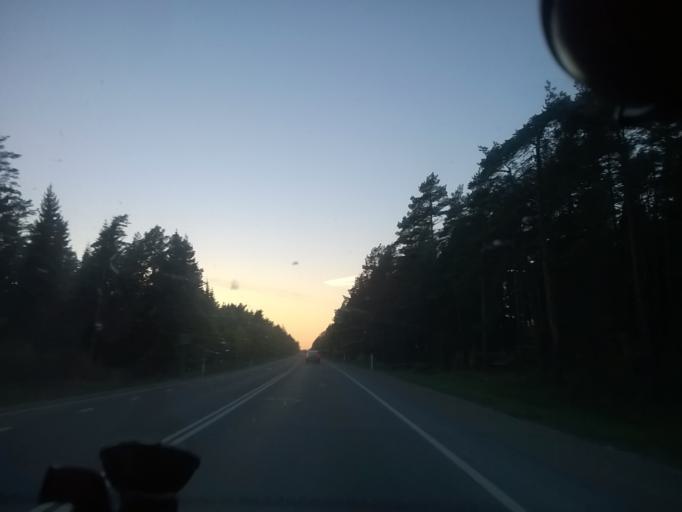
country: EE
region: Laeaene
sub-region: Lihula vald
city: Lihula
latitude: 58.9739
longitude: 23.9255
